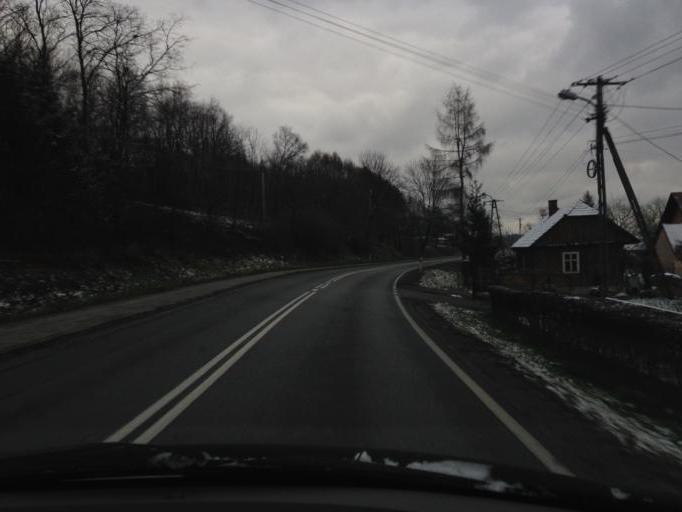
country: PL
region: Lesser Poland Voivodeship
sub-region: Powiat brzeski
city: Zlota
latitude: 49.8609
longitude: 20.7147
